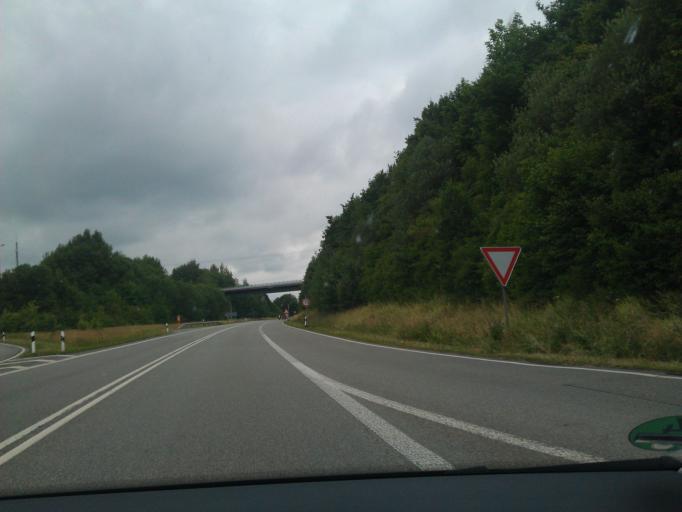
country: DE
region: Rheinland-Pfalz
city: Weselberg
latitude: 49.3300
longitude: 7.6067
